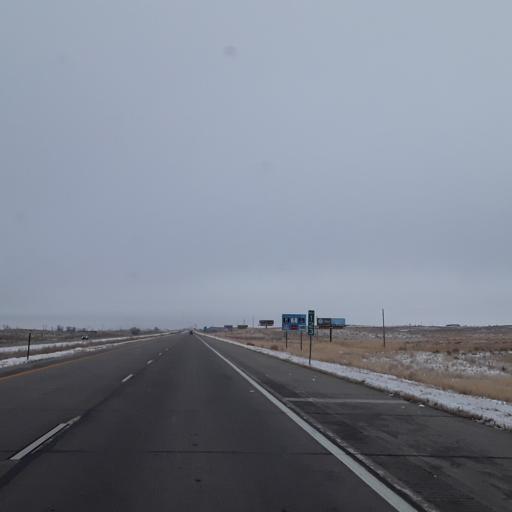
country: US
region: Colorado
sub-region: Logan County
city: Sterling
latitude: 40.5972
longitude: -103.1867
